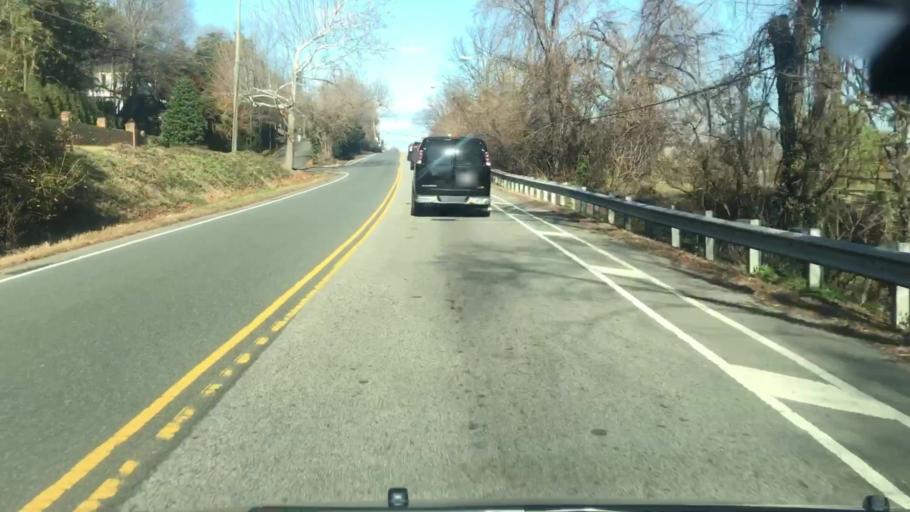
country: US
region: Virginia
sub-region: Fairfax County
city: Belle Haven
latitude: 38.7829
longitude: -77.0614
